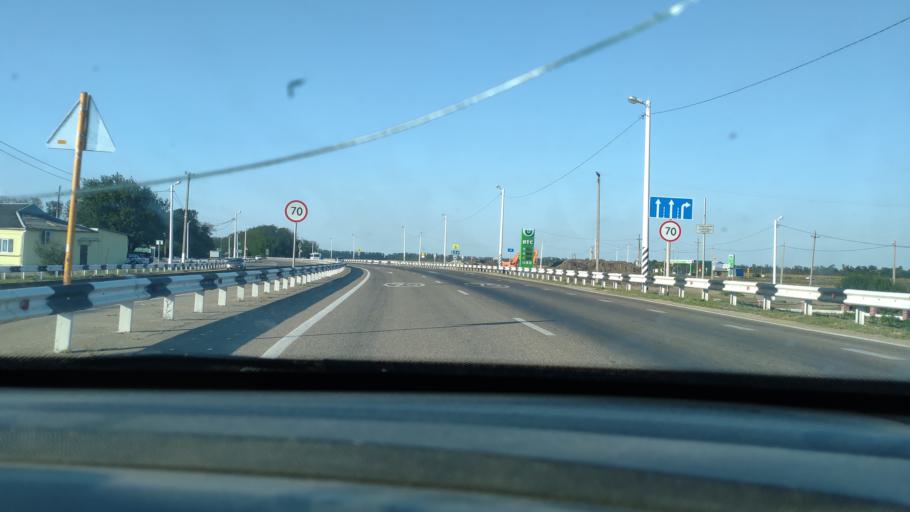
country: RU
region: Krasnodarskiy
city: Timashevsk
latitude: 45.5199
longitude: 38.9414
